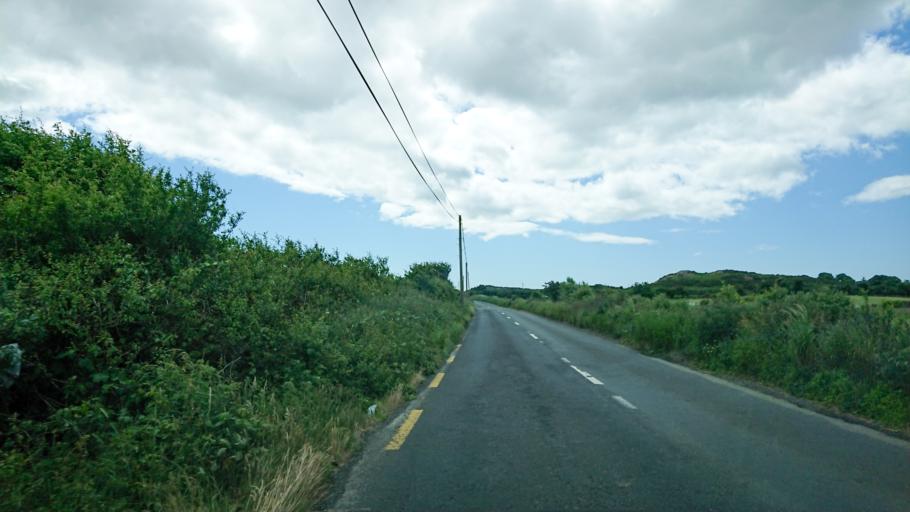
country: IE
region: Munster
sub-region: Waterford
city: Tra Mhor
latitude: 52.1880
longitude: -7.1793
